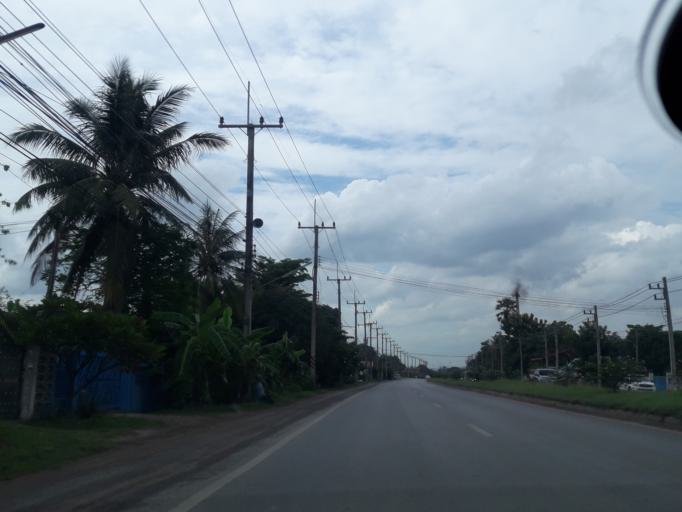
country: TH
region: Sara Buri
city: Kaeng Khoi
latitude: 14.5482
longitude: 101.0071
